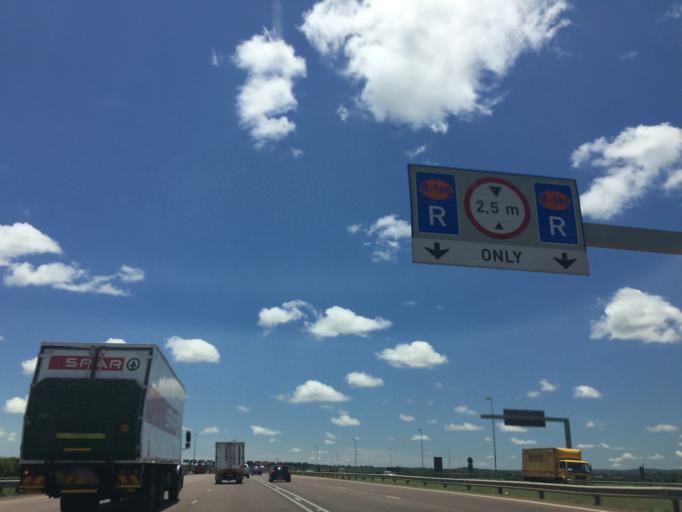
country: ZA
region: Gauteng
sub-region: City of Tshwane Metropolitan Municipality
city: Pretoria
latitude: -25.6434
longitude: 28.2495
